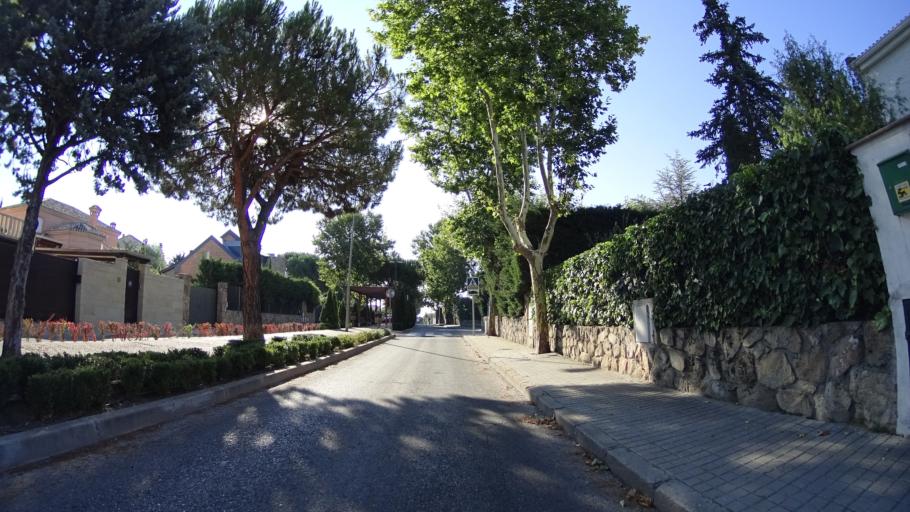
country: ES
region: Madrid
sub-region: Provincia de Madrid
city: Torrelodones
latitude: 40.5795
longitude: -3.9247
